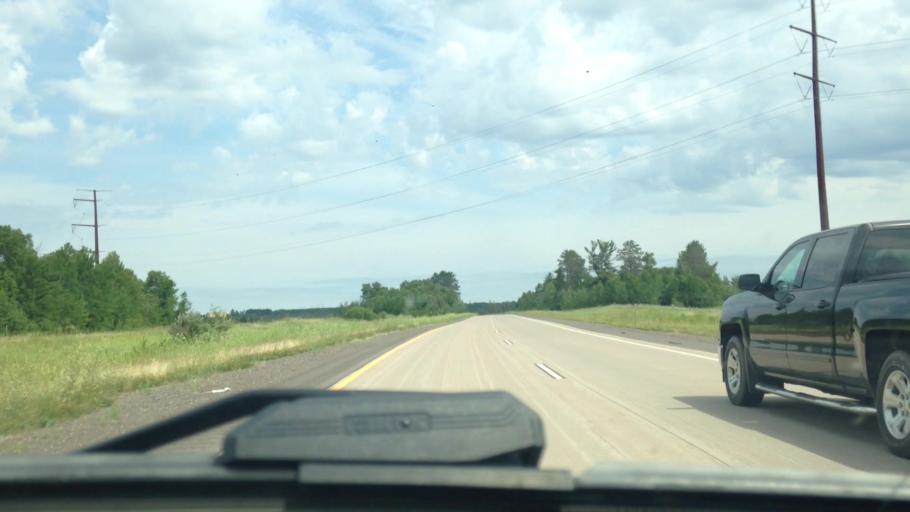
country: US
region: Wisconsin
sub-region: Douglas County
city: Lake Nebagamon
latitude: 46.2557
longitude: -91.8016
